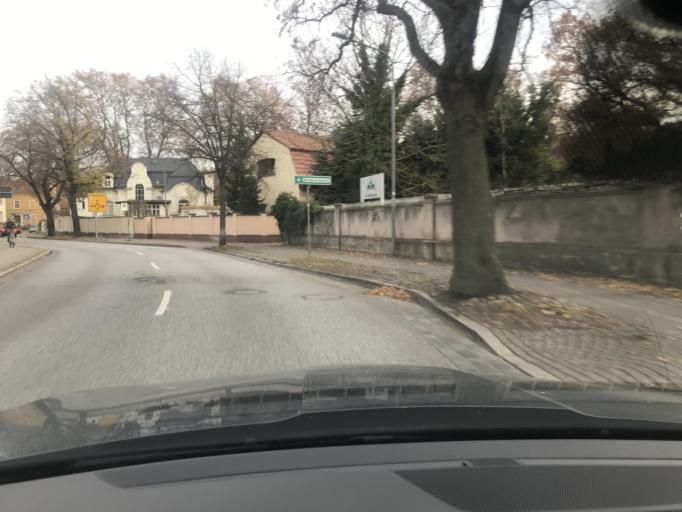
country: DE
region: Saxony-Anhalt
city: Quedlinburg
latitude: 51.7842
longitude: 11.1381
